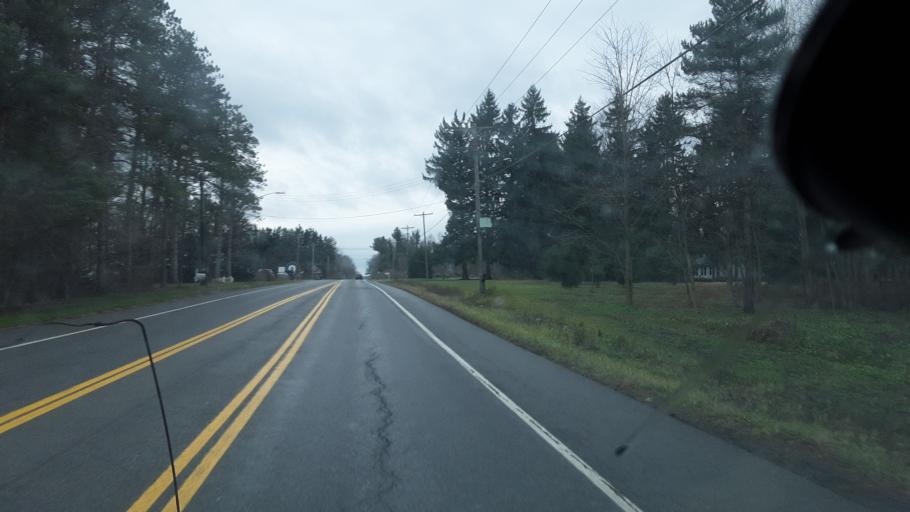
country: US
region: New York
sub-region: Erie County
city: Holland
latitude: 42.6731
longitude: -78.5606
